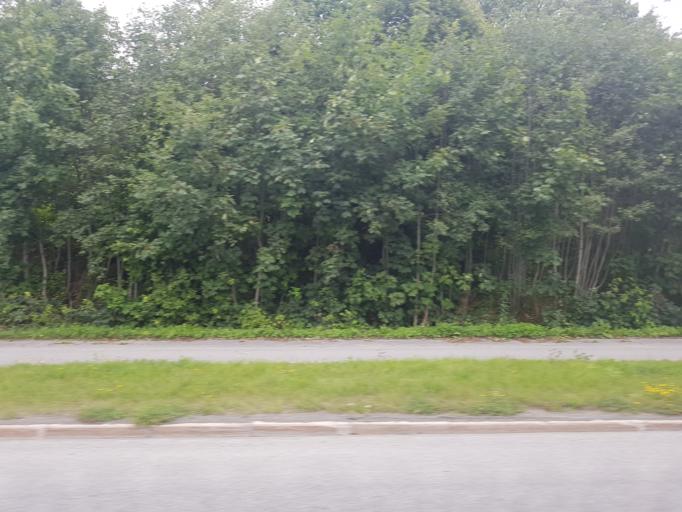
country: NO
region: Sor-Trondelag
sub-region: Trondheim
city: Trondheim
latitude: 63.3902
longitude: 10.3966
